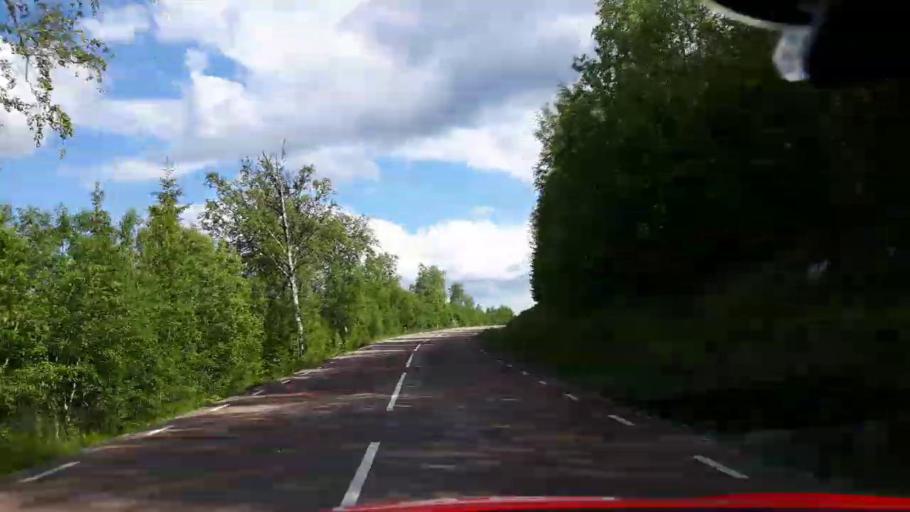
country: SE
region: Jaemtland
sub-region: Krokoms Kommun
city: Valla
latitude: 63.9504
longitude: 14.2158
